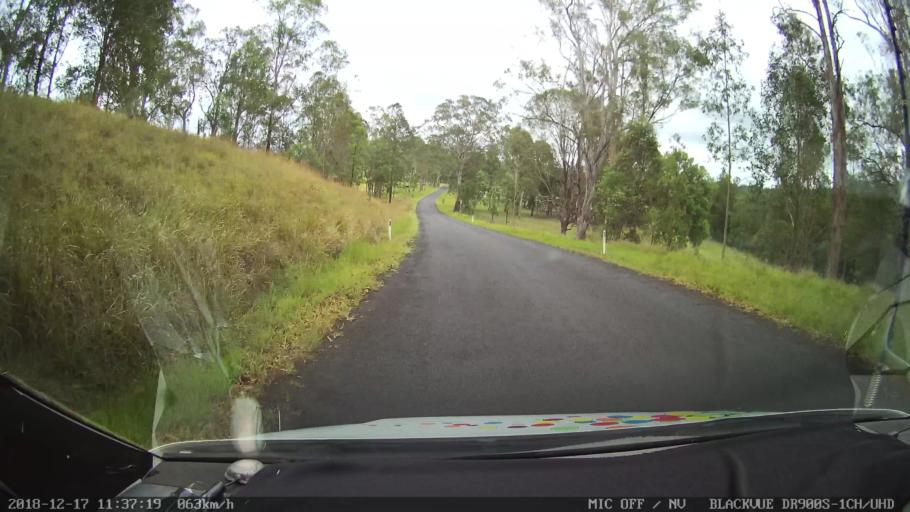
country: AU
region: New South Wales
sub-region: Kyogle
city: Kyogle
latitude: -28.7053
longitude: 152.6056
